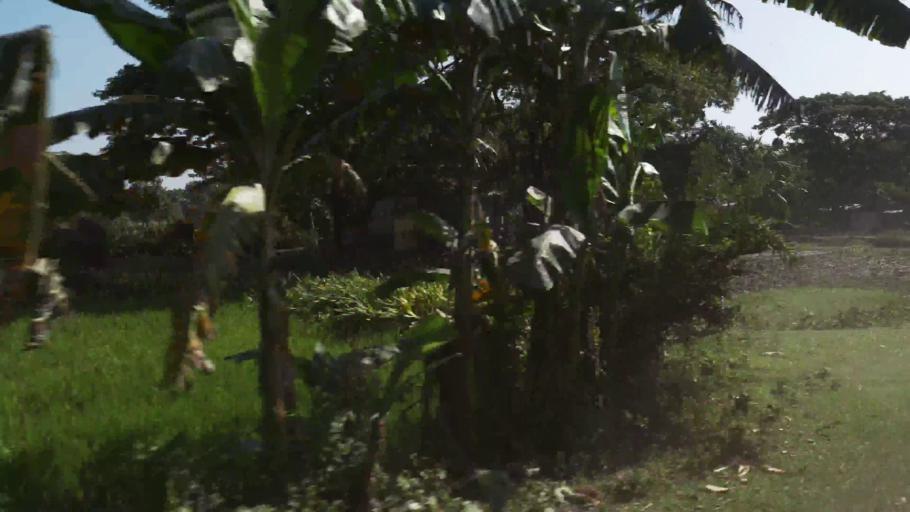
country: BD
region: Dhaka
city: Gafargaon
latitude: 24.5305
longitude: 90.5086
